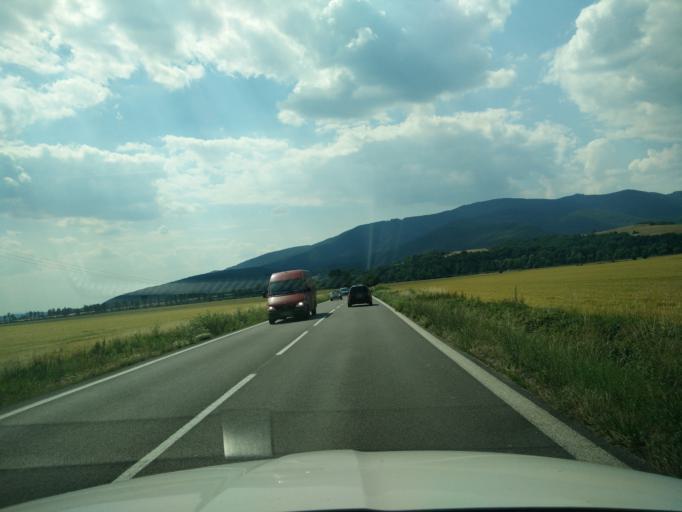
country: SK
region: Nitriansky
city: Novaky
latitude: 48.7220
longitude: 18.4932
